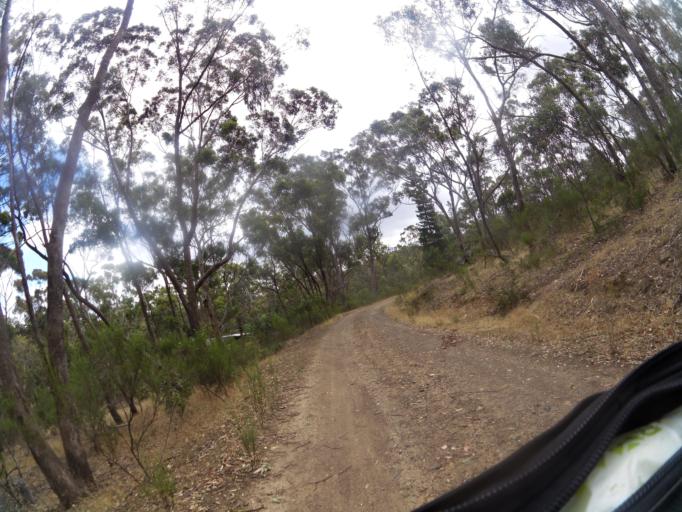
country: AU
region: Victoria
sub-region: Mount Alexander
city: Castlemaine
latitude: -37.0330
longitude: 144.2634
